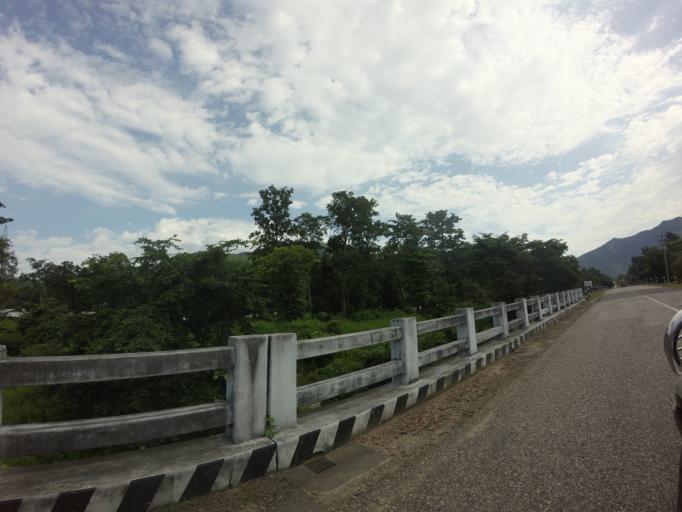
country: NP
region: Far Western
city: Tikapur
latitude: 28.6223
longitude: 81.2458
